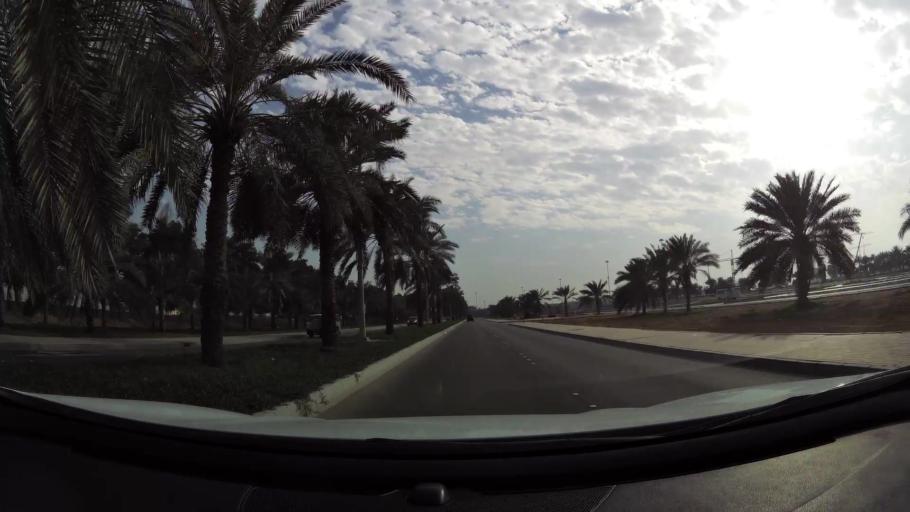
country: AE
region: Abu Dhabi
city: Abu Dhabi
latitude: 24.4105
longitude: 54.4805
